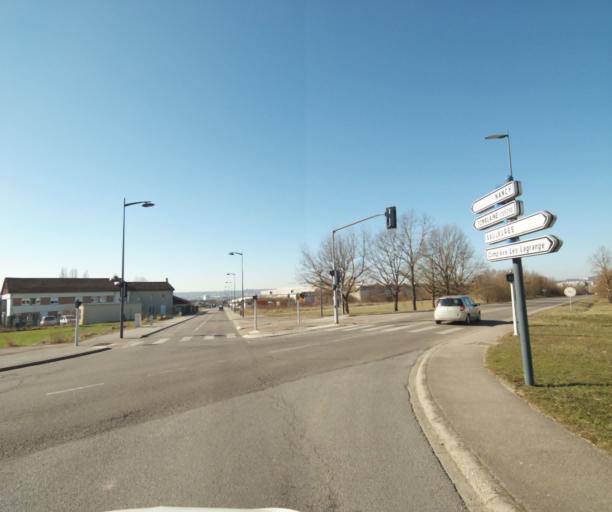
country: FR
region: Lorraine
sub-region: Departement de Meurthe-et-Moselle
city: Tomblaine
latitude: 48.6757
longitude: 6.2275
